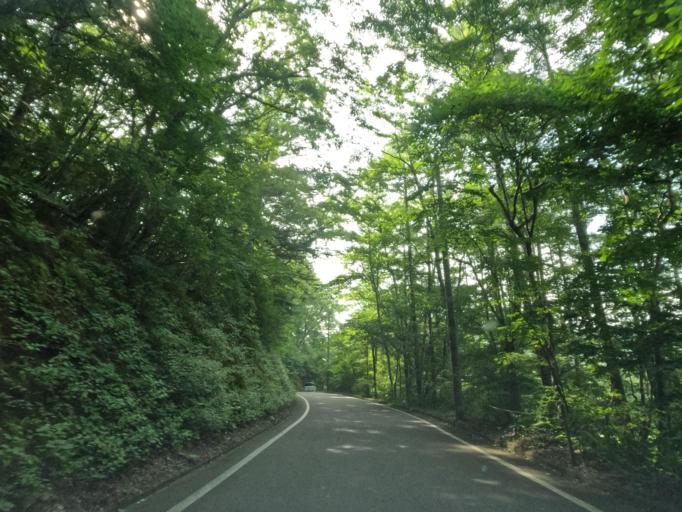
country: JP
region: Nagano
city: Komoro
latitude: 36.3580
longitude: 138.6218
